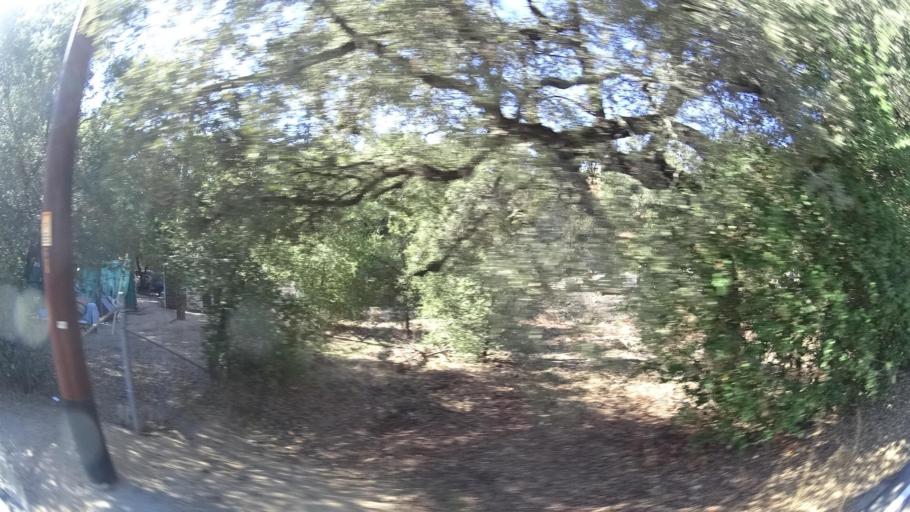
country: MX
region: Baja California
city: Tecate
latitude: 32.6737
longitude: -116.7091
